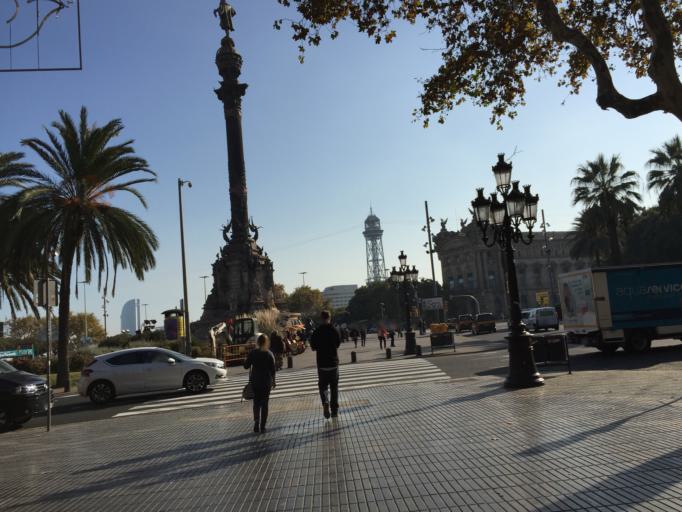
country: ES
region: Catalonia
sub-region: Provincia de Barcelona
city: Ciutat Vella
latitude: 41.3764
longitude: 2.1770
